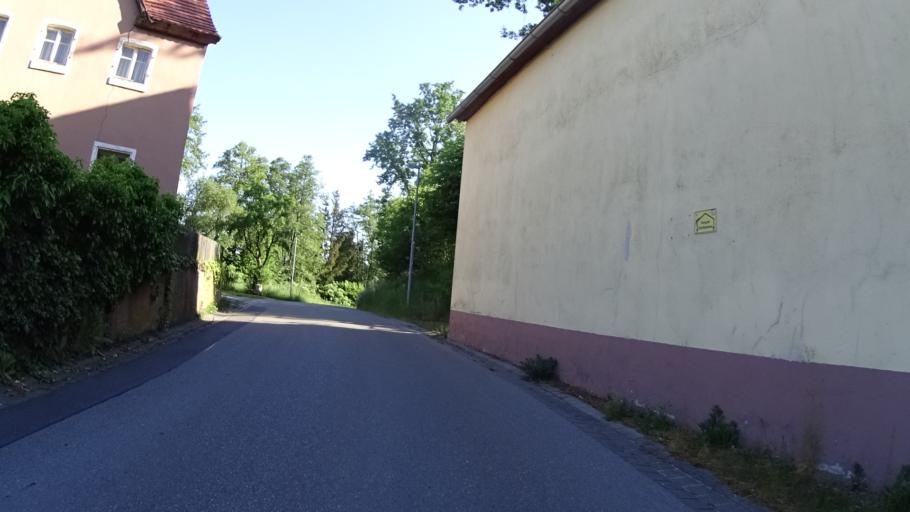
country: DE
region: Bavaria
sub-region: Regierungsbezirk Mittelfranken
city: Wieseth
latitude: 49.1565
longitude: 10.4664
